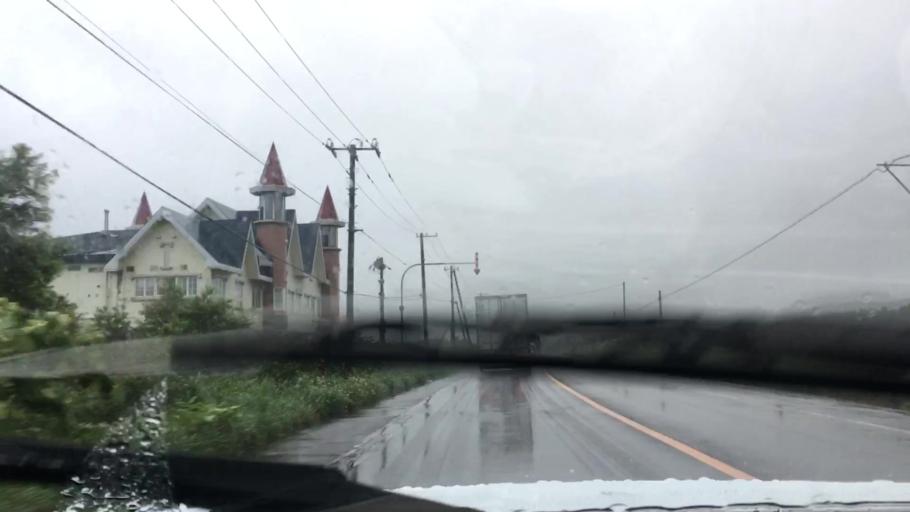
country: JP
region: Hokkaido
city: Niseko Town
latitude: 42.4703
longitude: 140.3432
